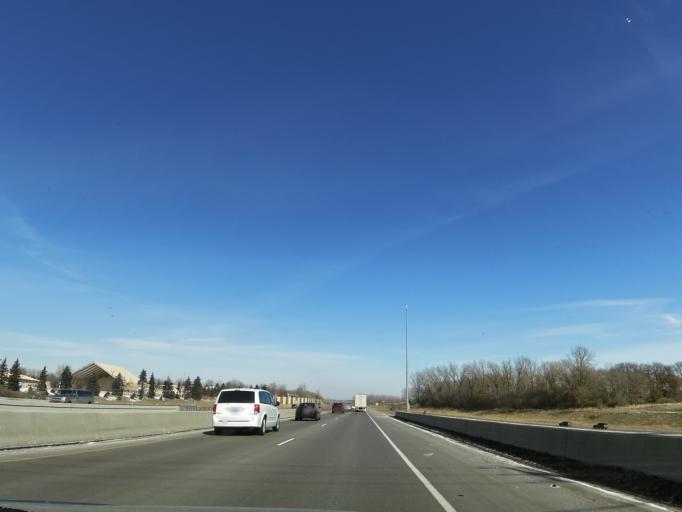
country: US
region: Minnesota
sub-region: Washington County
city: Oakdale
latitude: 44.9973
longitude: -92.9592
